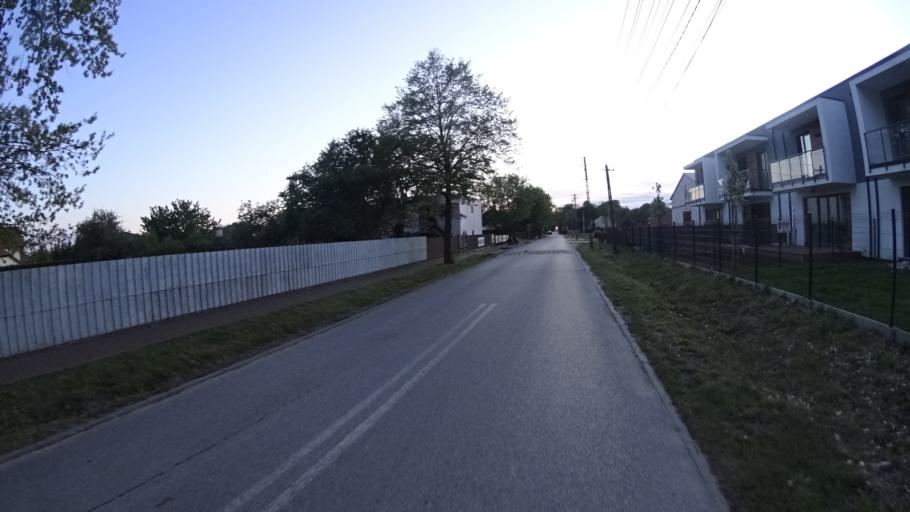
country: PL
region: Masovian Voivodeship
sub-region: Powiat warszawski zachodni
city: Ozarow Mazowiecki
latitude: 52.2144
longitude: 20.7830
